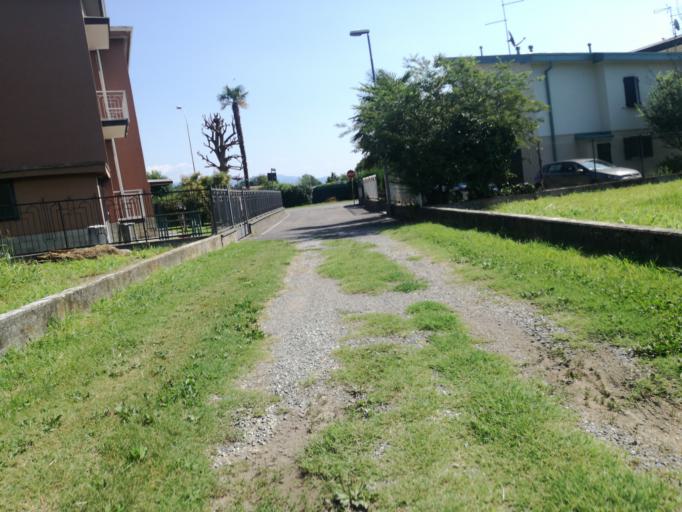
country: IT
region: Lombardy
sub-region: Provincia di Bergamo
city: Solza
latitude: 45.6834
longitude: 9.4809
